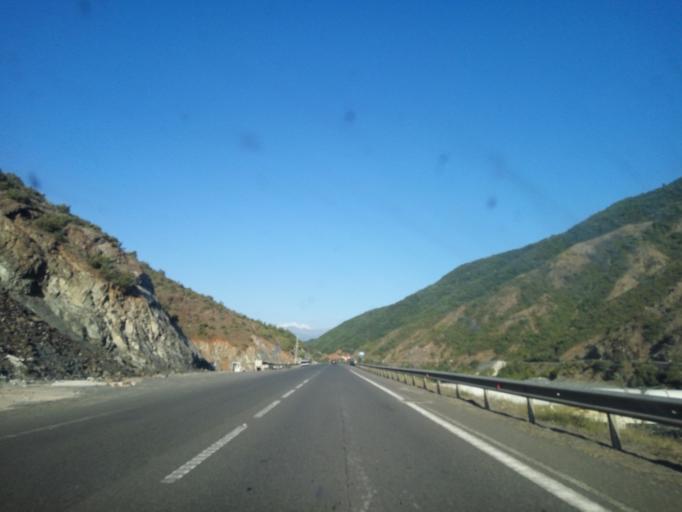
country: AL
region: Lezhe
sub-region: Rrethi i Mirdites
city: Rreshen
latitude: 41.7813
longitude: 19.8338
